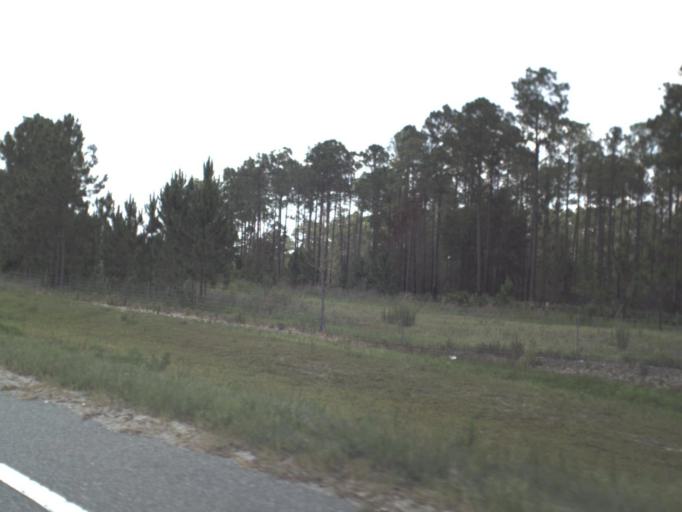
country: US
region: Florida
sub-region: Bradford County
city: Starke
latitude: 29.9973
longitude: -82.0301
